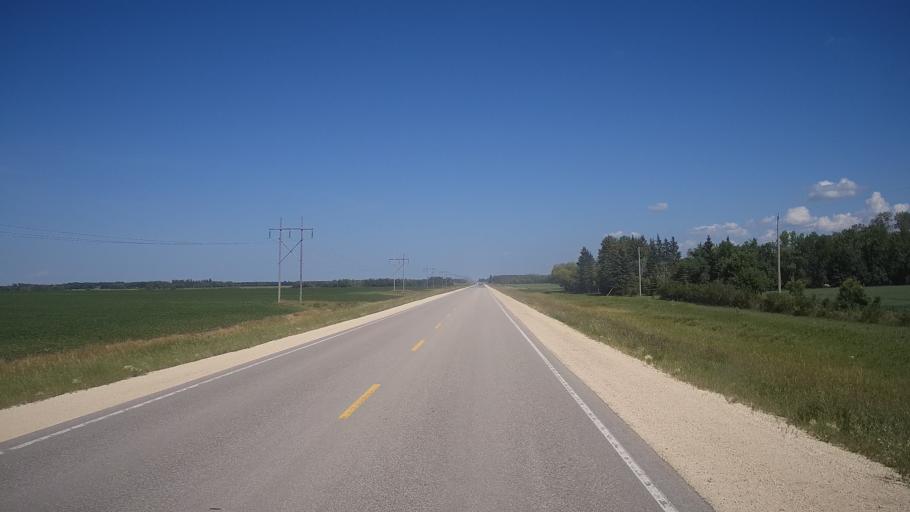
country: CA
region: Manitoba
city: Stonewall
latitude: 50.1227
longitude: -97.3829
